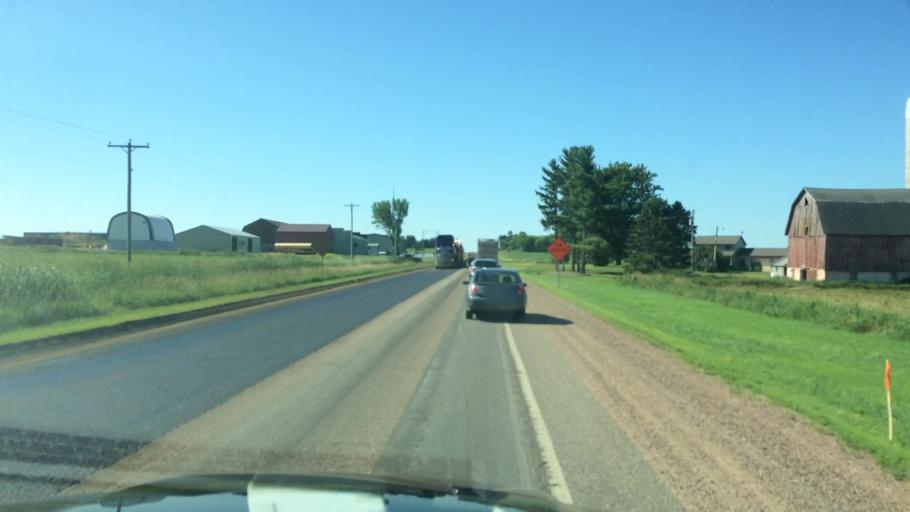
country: US
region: Wisconsin
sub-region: Marathon County
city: Stratford
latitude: 44.8950
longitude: -90.0788
